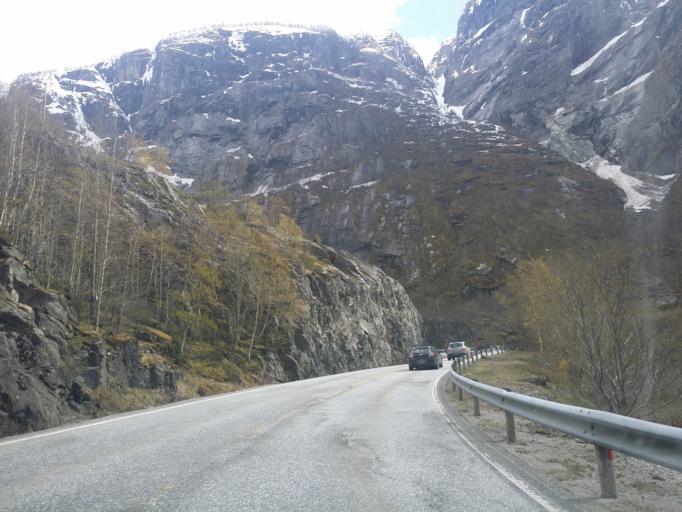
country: NO
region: Hordaland
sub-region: Eidfjord
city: Eidfjord
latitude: 60.4187
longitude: 7.1923
